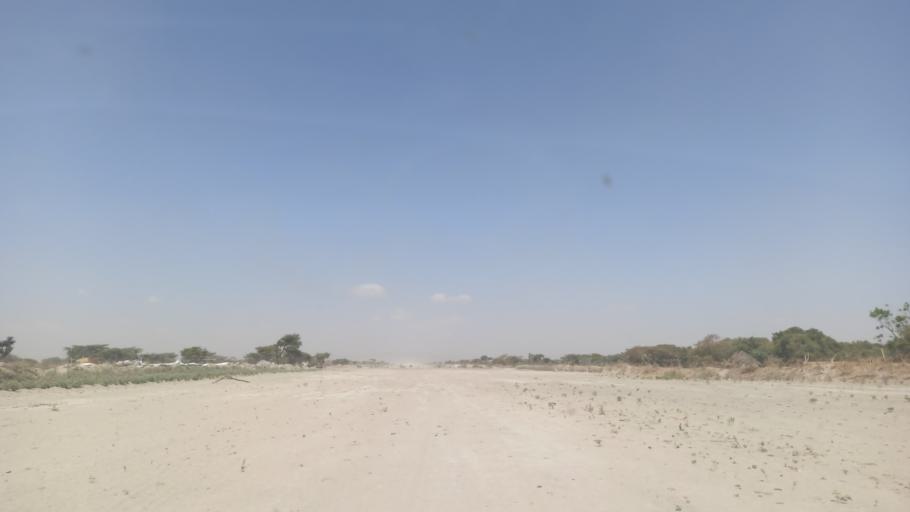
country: ET
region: Oromiya
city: Ziway
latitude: 7.7060
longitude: 38.6385
